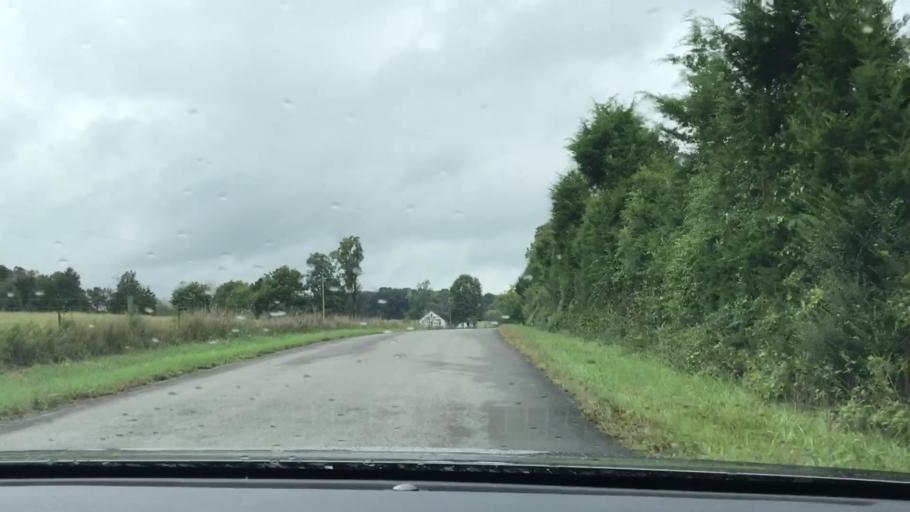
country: US
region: Tennessee
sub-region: Macon County
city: Red Boiling Springs
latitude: 36.6138
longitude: -85.7713
